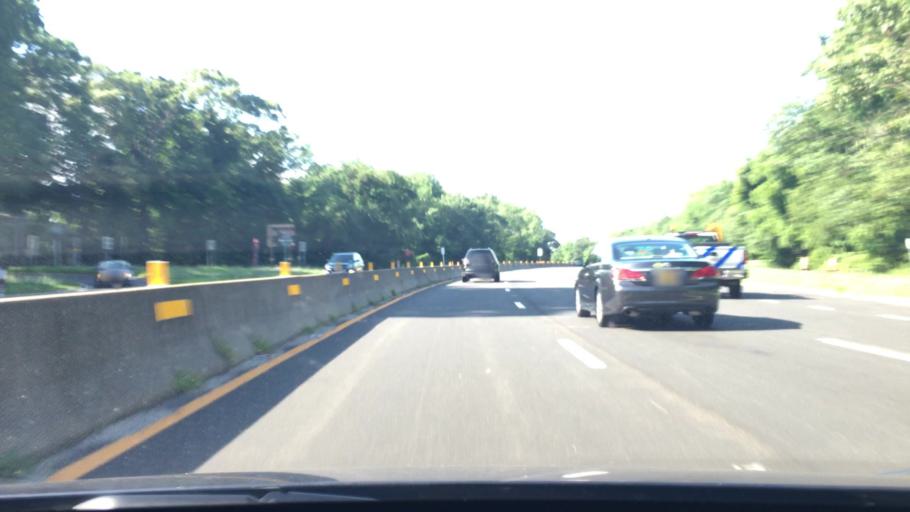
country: US
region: New York
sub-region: Nassau County
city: Bellmore
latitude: 40.6711
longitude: -73.5145
